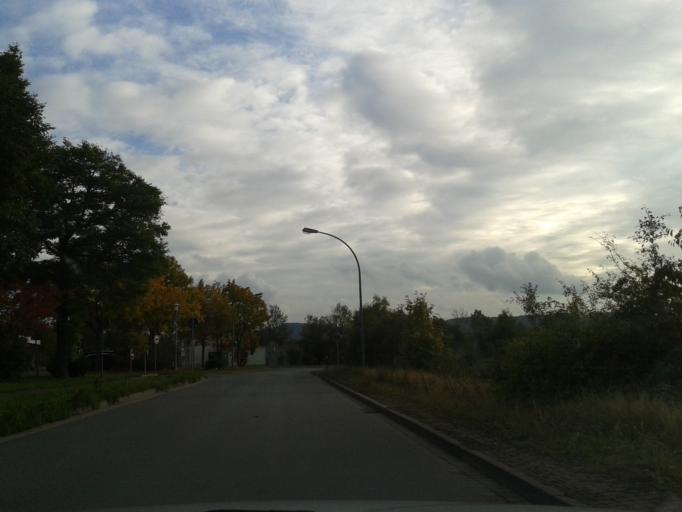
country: DE
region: North Rhine-Westphalia
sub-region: Regierungsbezirk Detmold
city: Horn-Bad Meinberg
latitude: 51.8824
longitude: 8.9541
